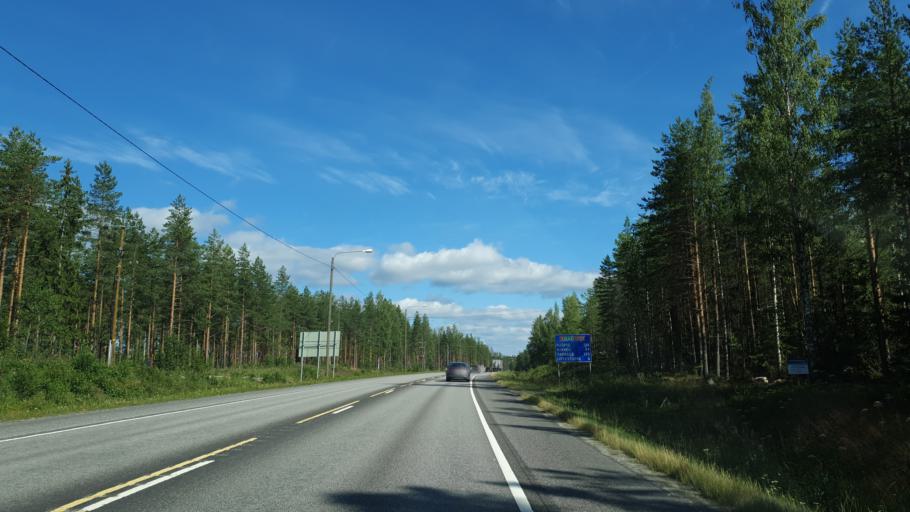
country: FI
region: Central Finland
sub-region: Jyvaeskylae
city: Toivakka
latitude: 62.2526
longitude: 26.1055
